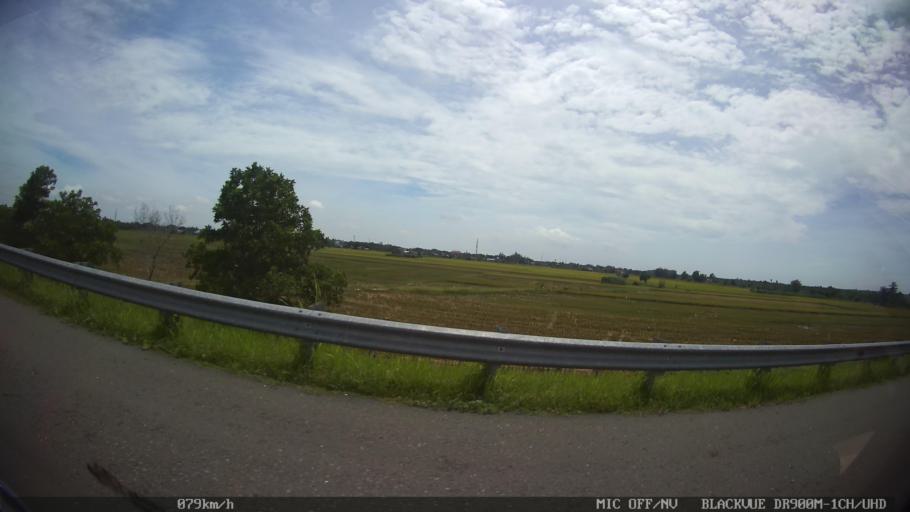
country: ID
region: North Sumatra
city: Percut
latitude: 3.5451
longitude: 98.8541
